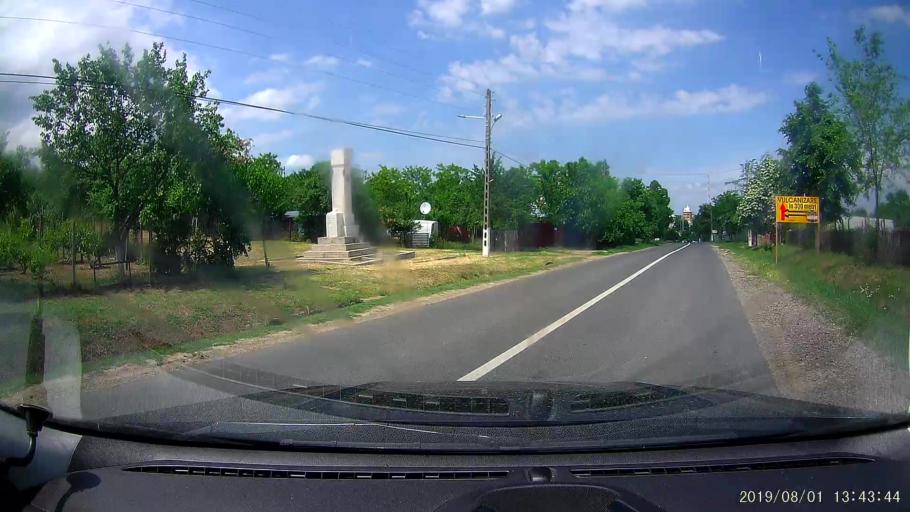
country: RO
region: Galati
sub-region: Comuna Oancea
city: Oancea
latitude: 45.9168
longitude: 28.1134
